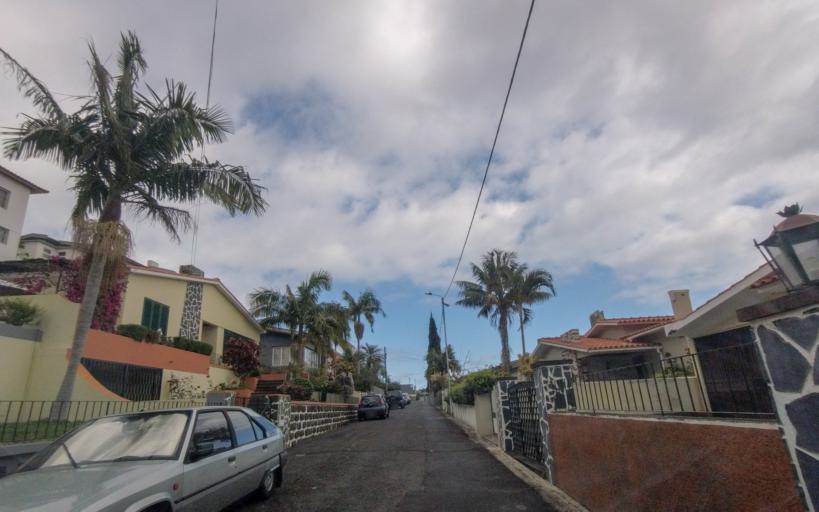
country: PT
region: Madeira
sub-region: Funchal
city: Nossa Senhora do Monte
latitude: 32.6629
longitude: -16.9070
